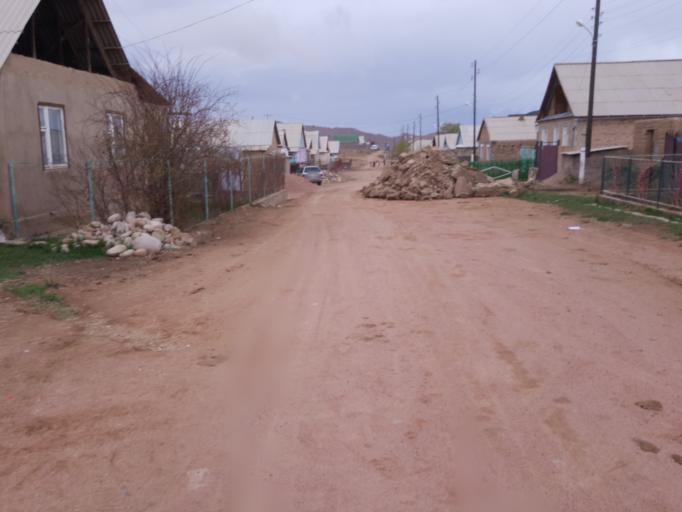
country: KG
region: Ysyk-Koel
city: Bokombayevskoye
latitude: 42.1089
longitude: 76.9808
